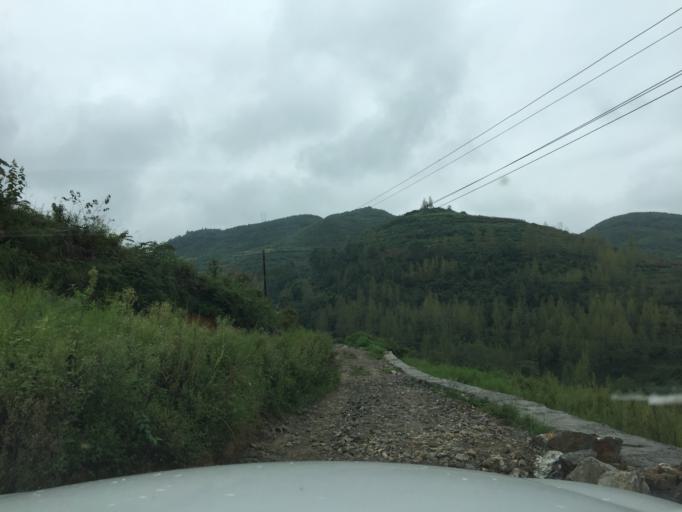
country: CN
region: Guizhou Sheng
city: Yantang
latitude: 28.2029
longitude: 108.0846
